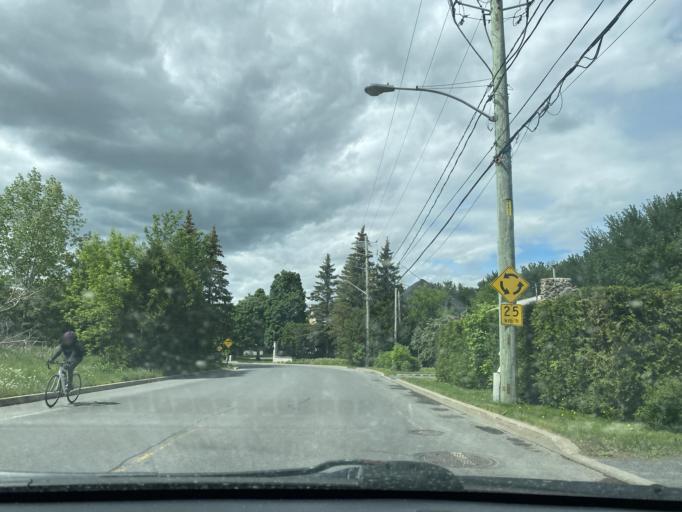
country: CA
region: Quebec
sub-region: Monteregie
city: Carignan
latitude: 45.4660
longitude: -73.2935
